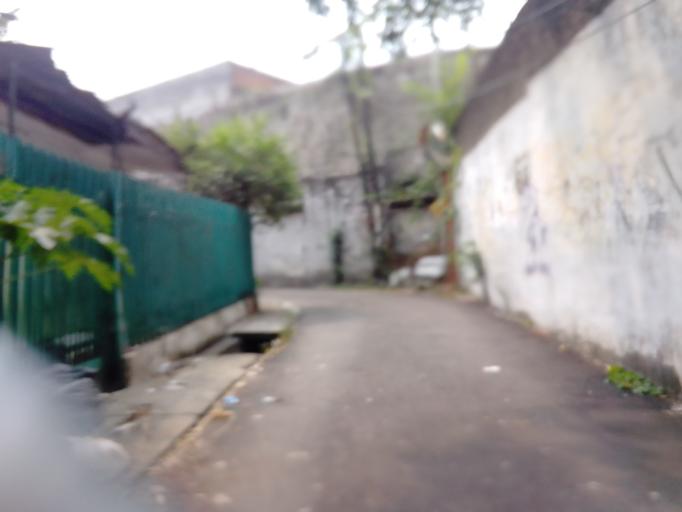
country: ID
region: Jakarta Raya
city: Jakarta
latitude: -6.2030
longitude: 106.8271
